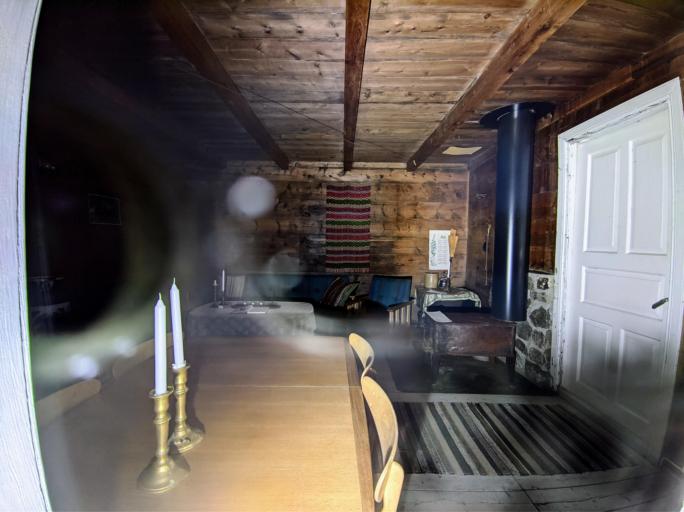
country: NO
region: Hordaland
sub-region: Eidfjord
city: Eidfjord
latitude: 60.5044
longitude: 7.1302
